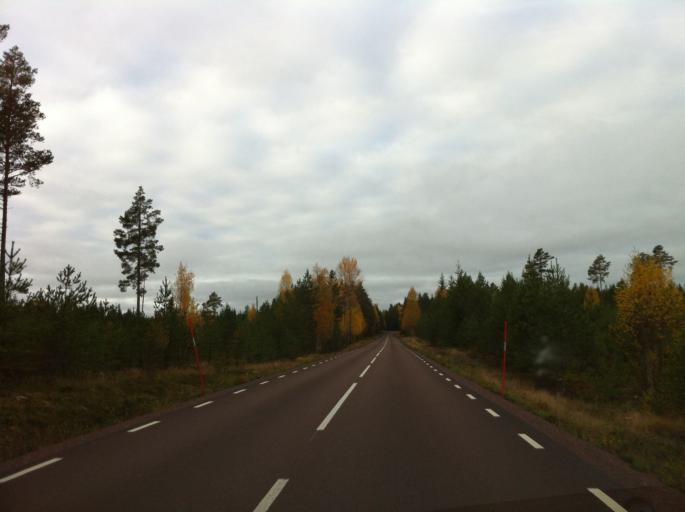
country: SE
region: Dalarna
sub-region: Orsa Kommun
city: Orsa
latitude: 61.1275
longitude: 14.5314
